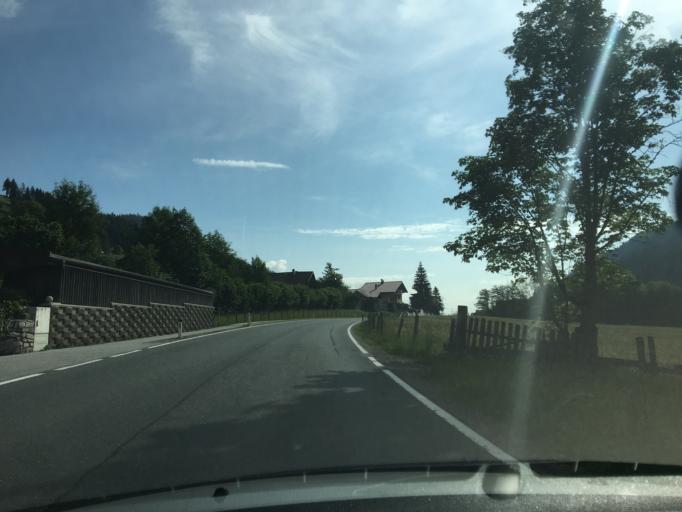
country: AT
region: Salzburg
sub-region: Politischer Bezirk Sankt Johann im Pongau
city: Wagrain
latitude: 47.3515
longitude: 13.3145
